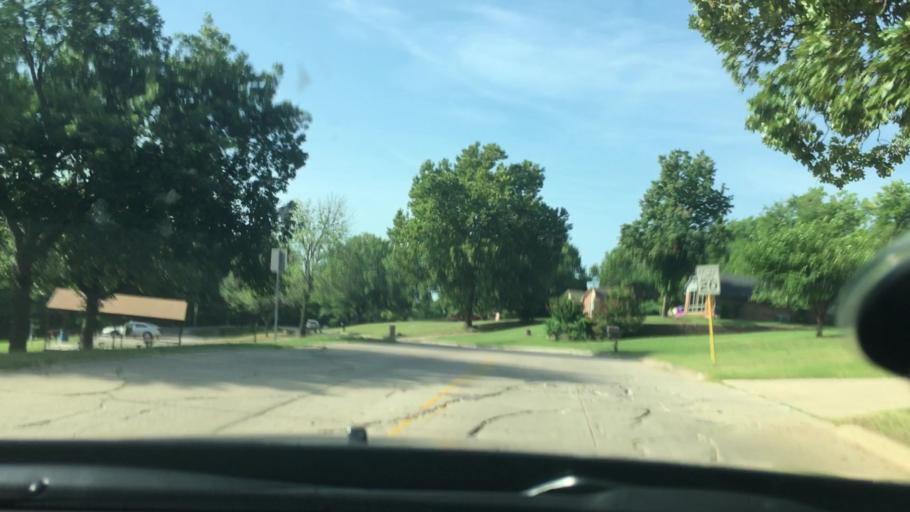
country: US
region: Oklahoma
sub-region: Pontotoc County
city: Ada
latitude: 34.7626
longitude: -96.6555
